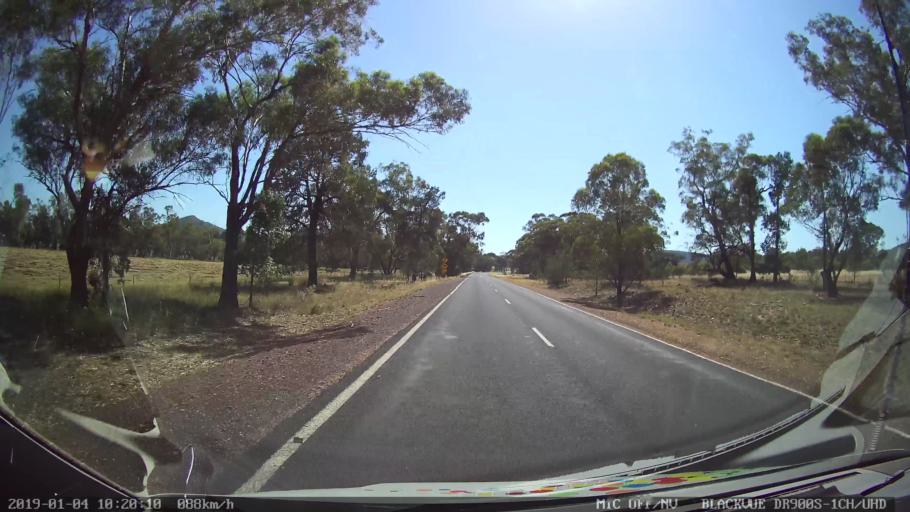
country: AU
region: New South Wales
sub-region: Cabonne
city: Canowindra
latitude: -33.3731
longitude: 148.4916
